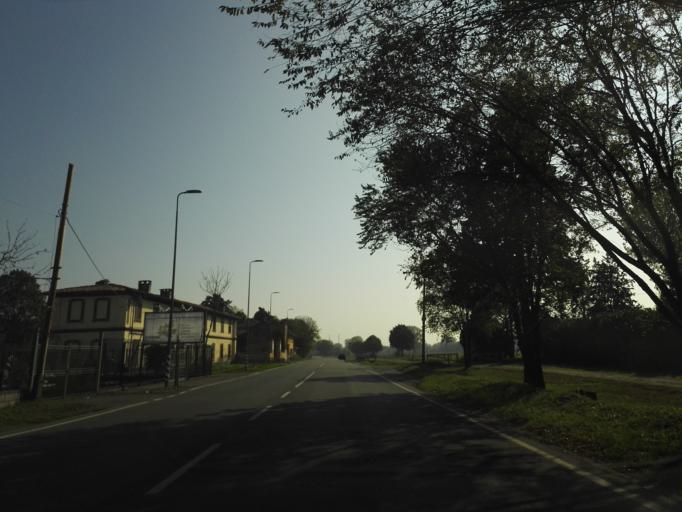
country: IT
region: Lombardy
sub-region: Citta metropolitana di Milano
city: Chiaravalle
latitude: 45.4260
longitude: 9.2305
